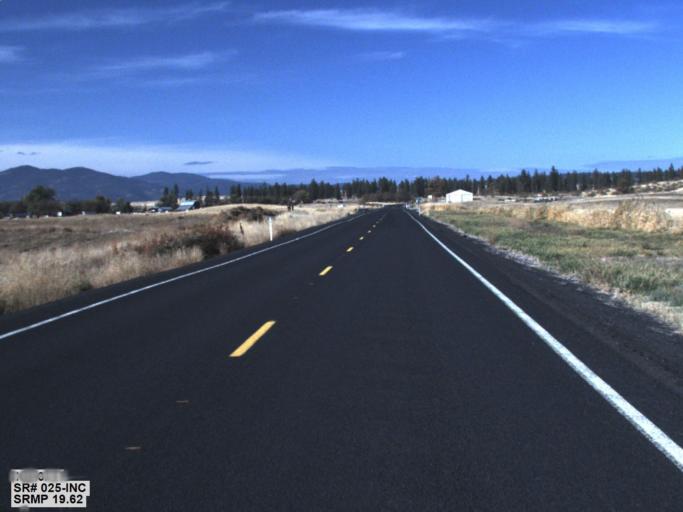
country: US
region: Washington
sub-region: Lincoln County
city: Davenport
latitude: 47.8896
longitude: -118.2676
